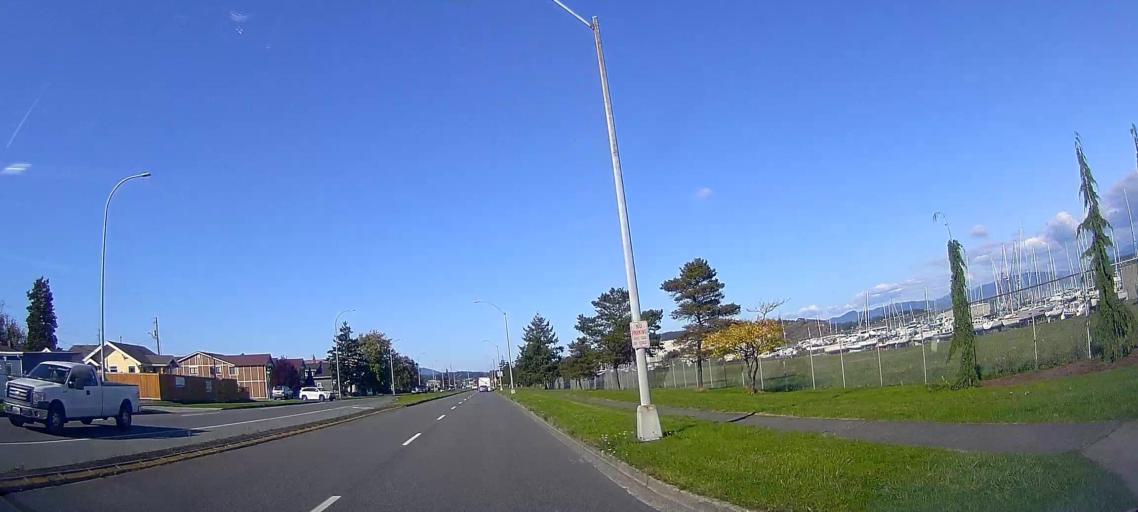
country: US
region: Washington
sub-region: Skagit County
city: Anacortes
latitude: 48.4998
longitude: -122.6095
